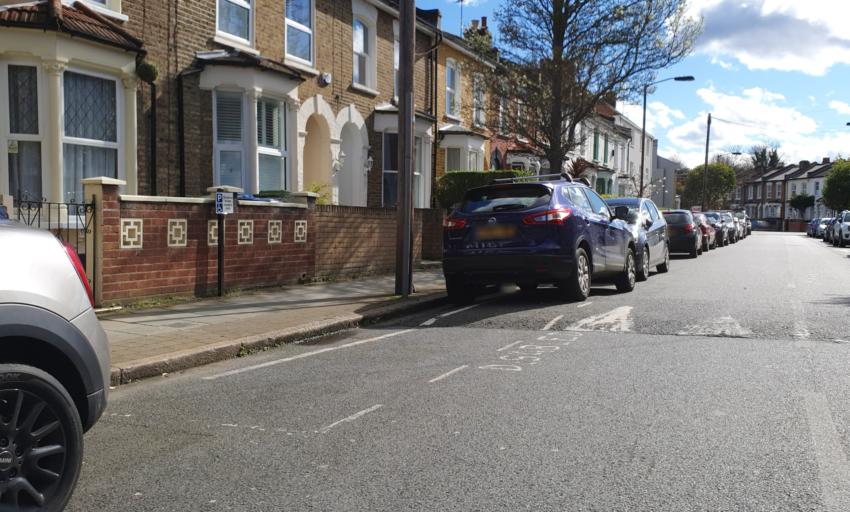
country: GB
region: England
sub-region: Greater London
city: Camberwell
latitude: 51.4691
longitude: -0.0558
